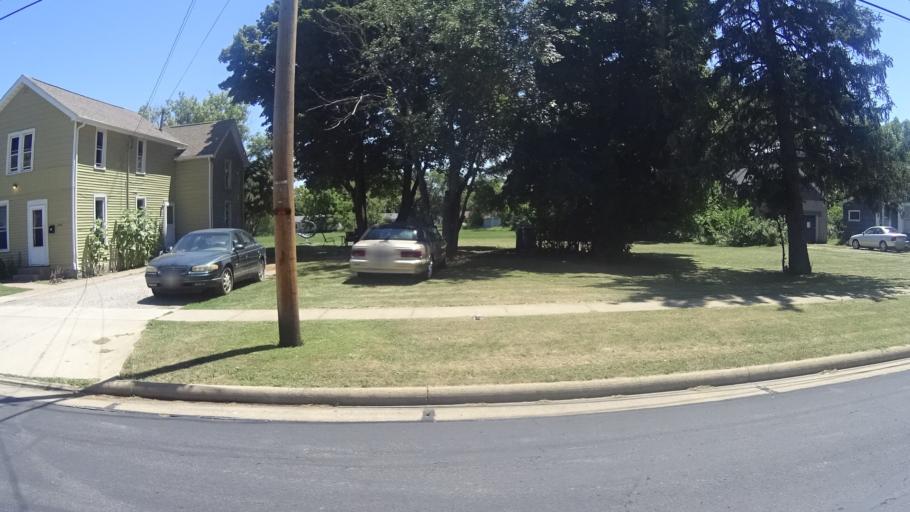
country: US
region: Ohio
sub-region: Erie County
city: Sandusky
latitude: 41.4401
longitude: -82.6895
